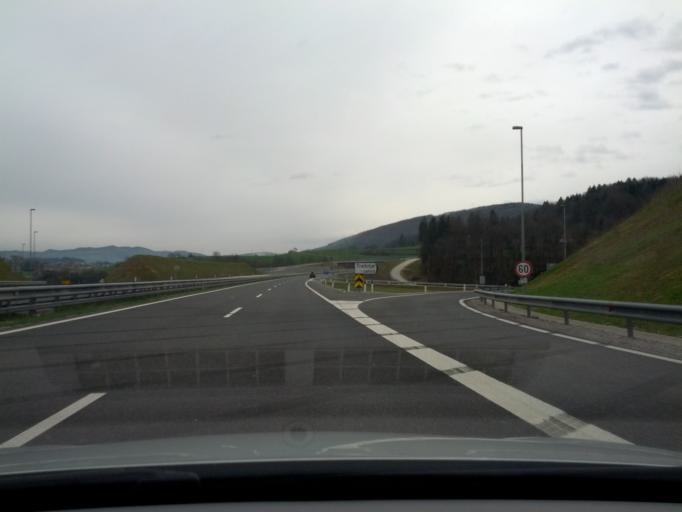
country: SI
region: Trebnje
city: Trebnje
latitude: 45.9101
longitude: 14.9652
